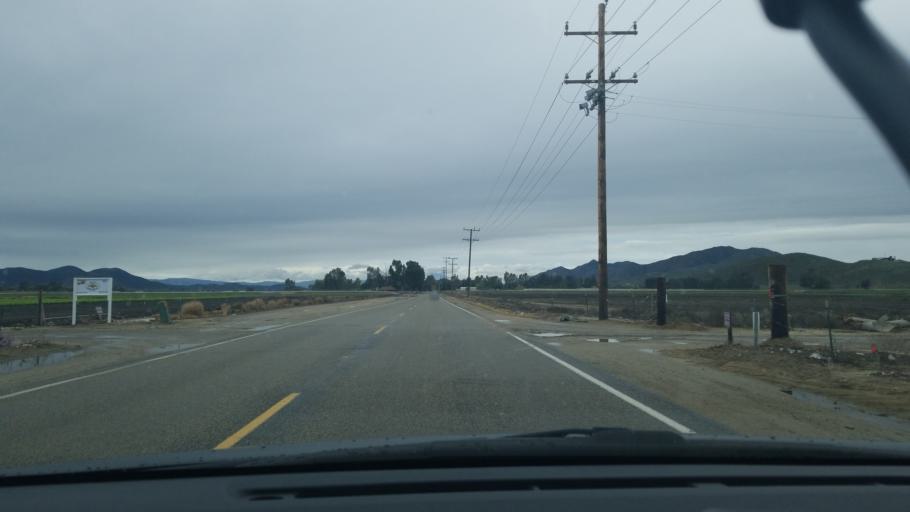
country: US
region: California
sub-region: Riverside County
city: Winchester
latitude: 33.7075
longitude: -117.0410
